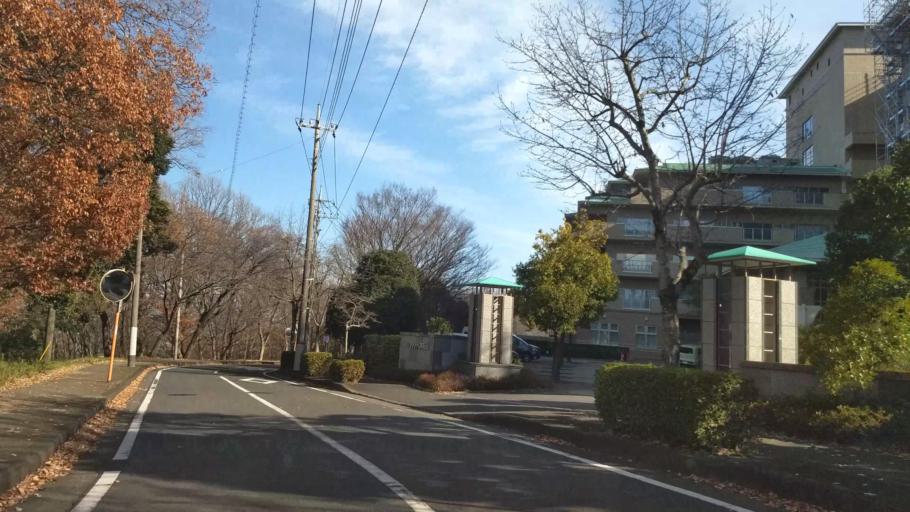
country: JP
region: Kanagawa
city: Hadano
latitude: 35.3557
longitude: 139.2294
